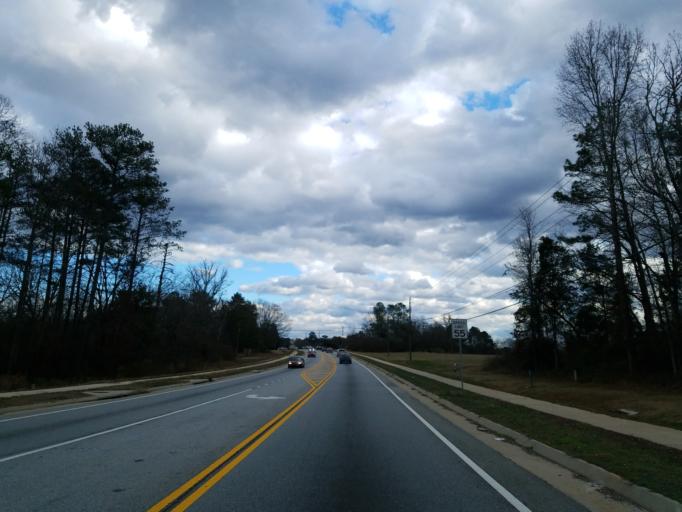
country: US
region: Georgia
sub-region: Henry County
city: McDonough
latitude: 33.4325
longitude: -84.1120
